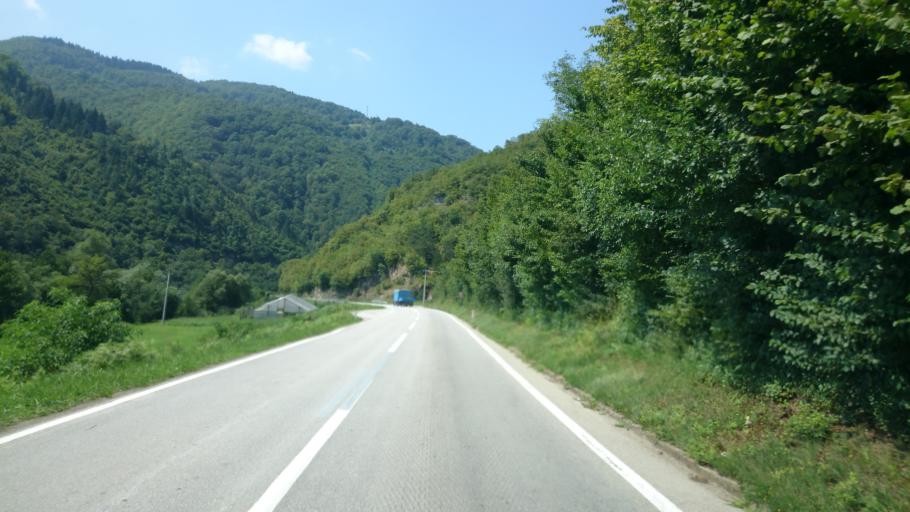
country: BA
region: Federation of Bosnia and Herzegovina
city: Donji Vakuf
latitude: 44.1844
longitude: 17.3487
